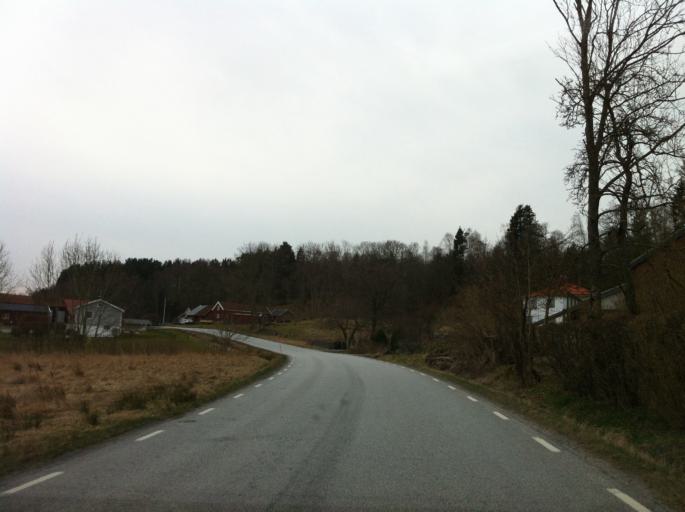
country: SE
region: Vaestra Goetaland
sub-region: Orust
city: Henan
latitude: 58.2428
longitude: 11.6814
